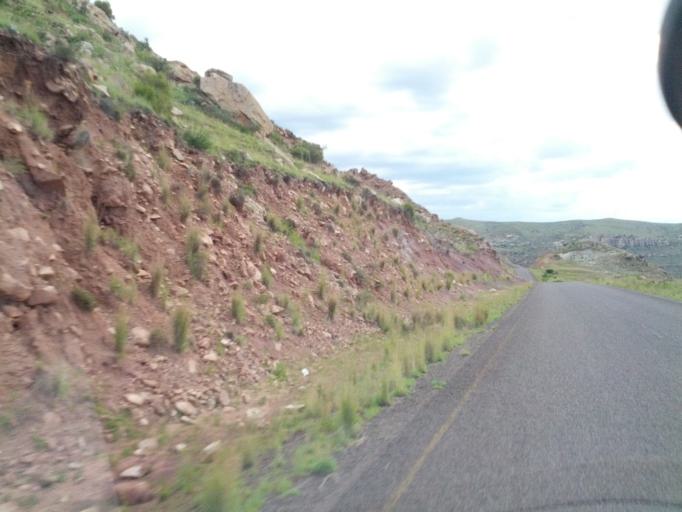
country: LS
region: Qacha's Nek
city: Qacha's Nek
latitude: -30.0630
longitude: 28.5273
